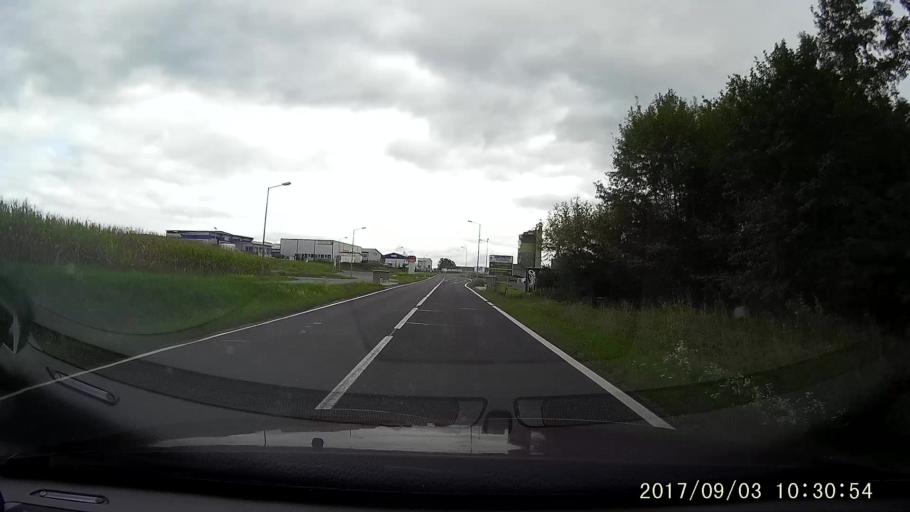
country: AT
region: Styria
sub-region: Politischer Bezirk Hartberg-Fuerstenfeld
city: Ilz
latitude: 47.0833
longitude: 15.9518
